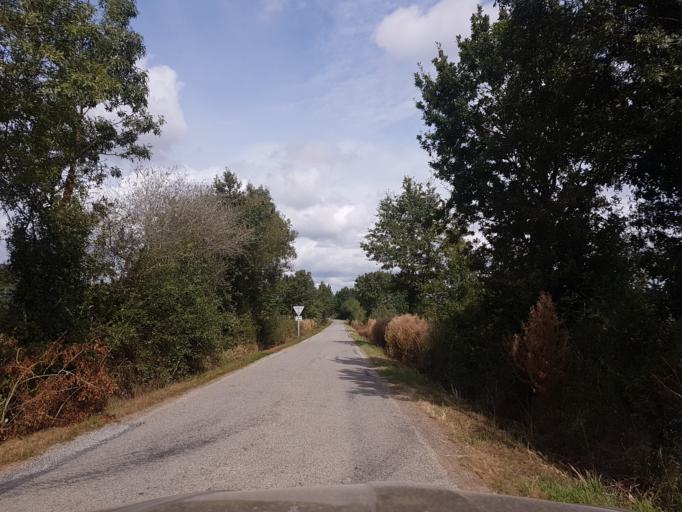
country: FR
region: Pays de la Loire
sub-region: Departement de la Loire-Atlantique
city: Petit-Mars
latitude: 47.4034
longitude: -1.4303
